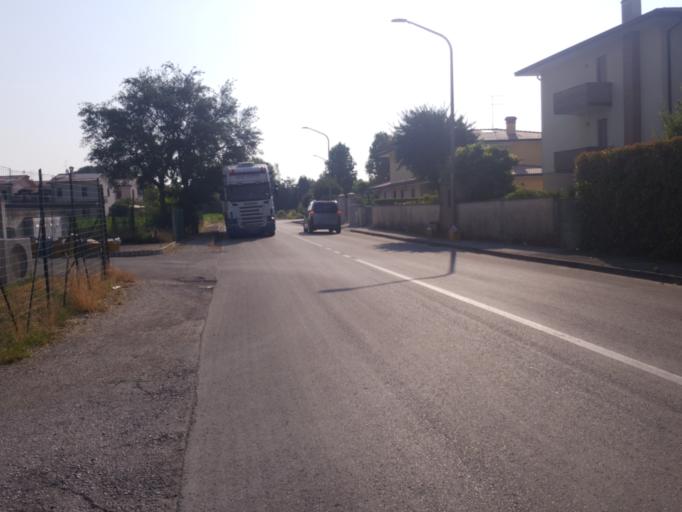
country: IT
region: Veneto
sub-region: Provincia di Vicenza
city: Torri di Quartesolo
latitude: 45.5249
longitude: 11.6393
